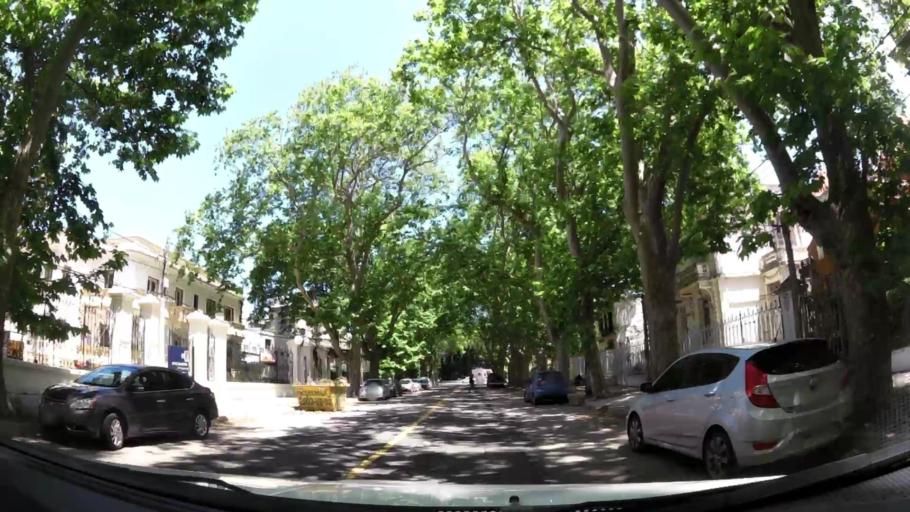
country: UY
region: Montevideo
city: Montevideo
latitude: -34.8685
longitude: -56.2045
